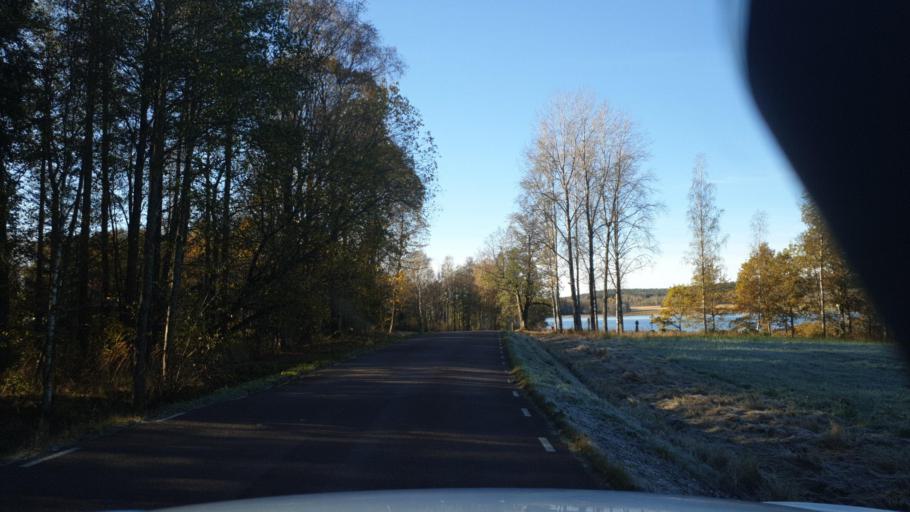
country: SE
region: Vaermland
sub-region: Karlstads Kommun
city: Valberg
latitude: 59.4326
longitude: 13.0869
